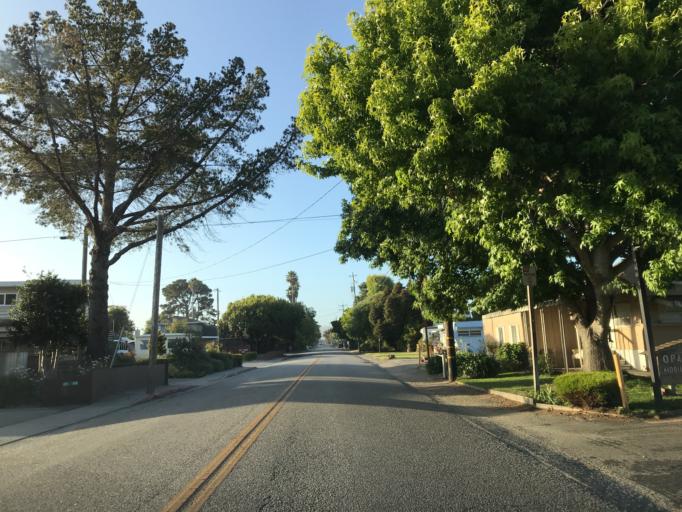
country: US
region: California
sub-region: Santa Cruz County
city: Opal Cliffs
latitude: 36.9644
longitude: -121.9674
